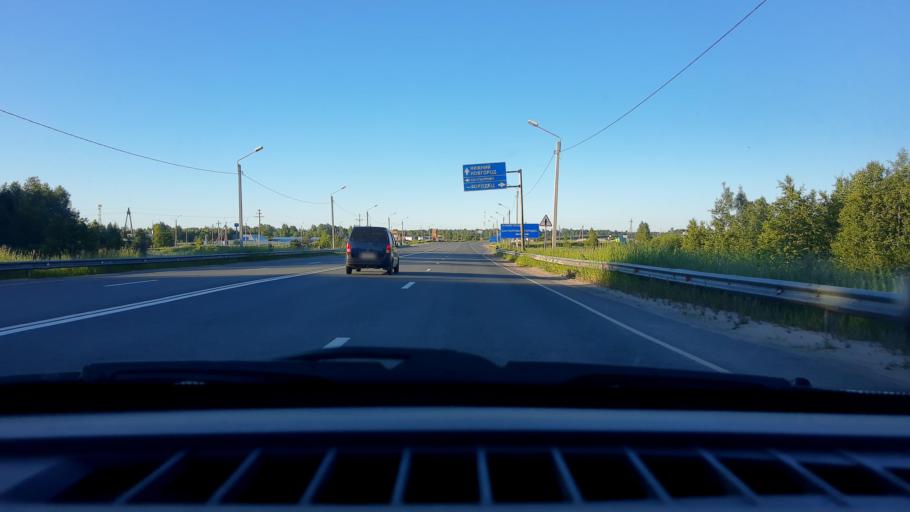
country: RU
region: Nizjnij Novgorod
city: Sitniki
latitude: 56.5046
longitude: 44.0240
